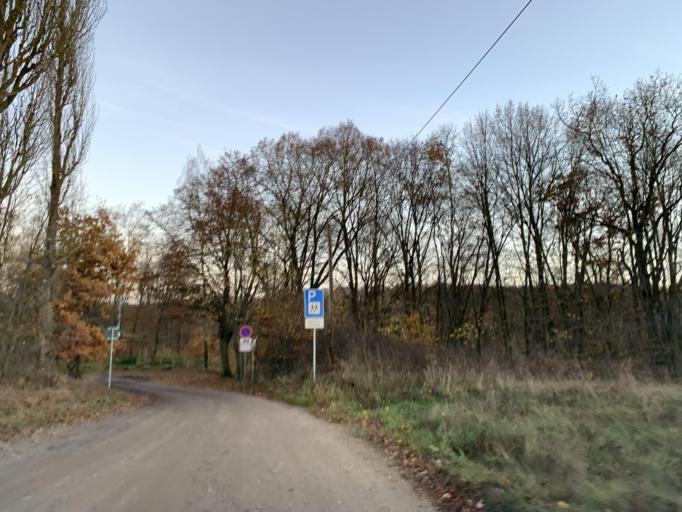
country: DE
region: Mecklenburg-Vorpommern
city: Loitz
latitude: 53.3268
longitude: 13.4405
